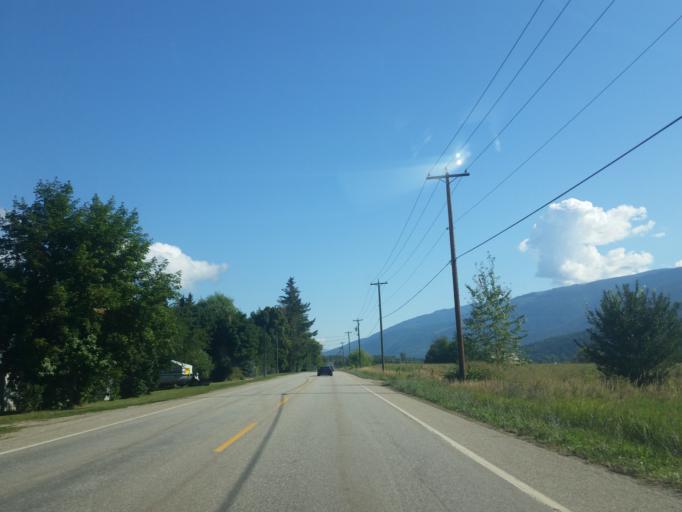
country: CA
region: British Columbia
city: Enderby
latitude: 50.6366
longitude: -119.1080
